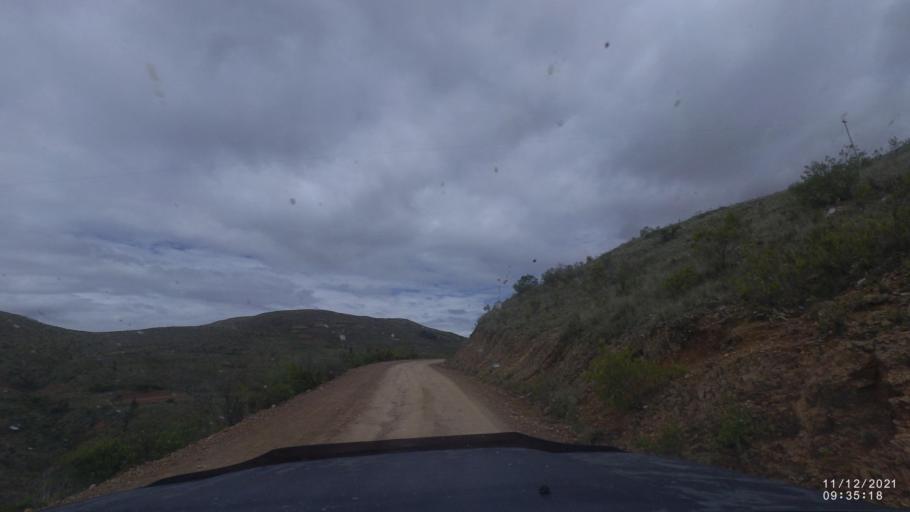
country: BO
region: Cochabamba
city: Tarata
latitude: -17.8286
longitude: -65.9899
